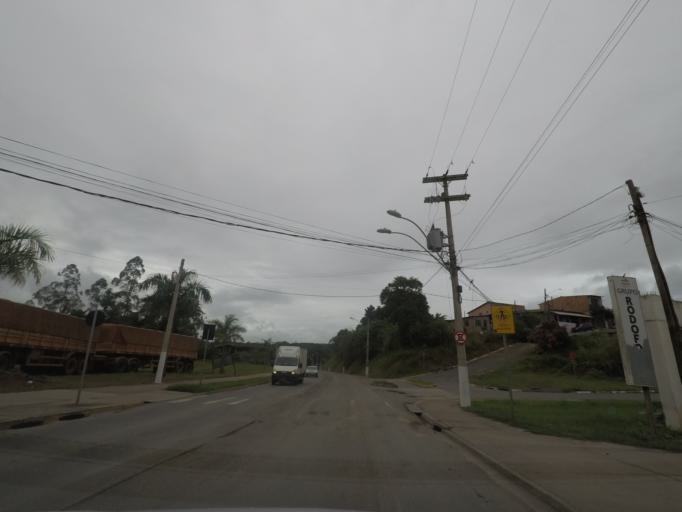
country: BR
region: Sao Paulo
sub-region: Cajati
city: Cajati
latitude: -24.7226
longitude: -48.0995
